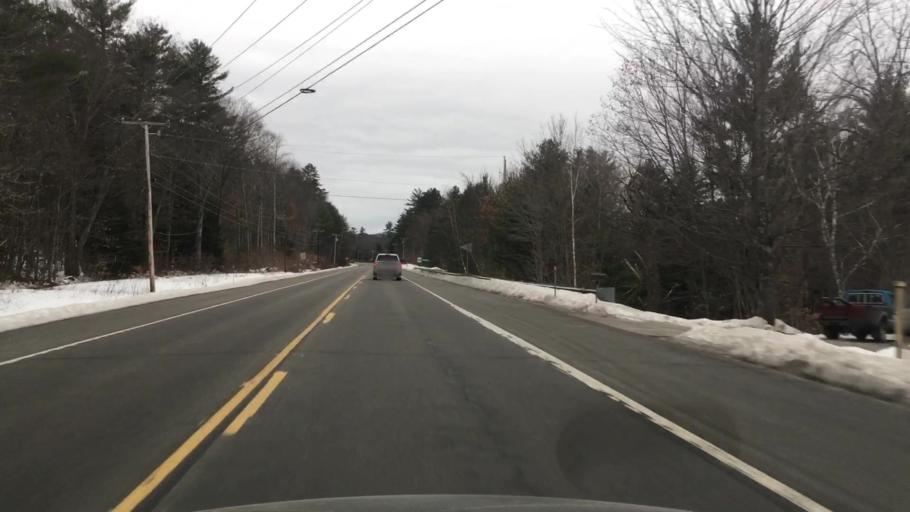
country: US
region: New Hampshire
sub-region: Merrimack County
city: Sutton
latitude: 43.2837
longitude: -71.9775
